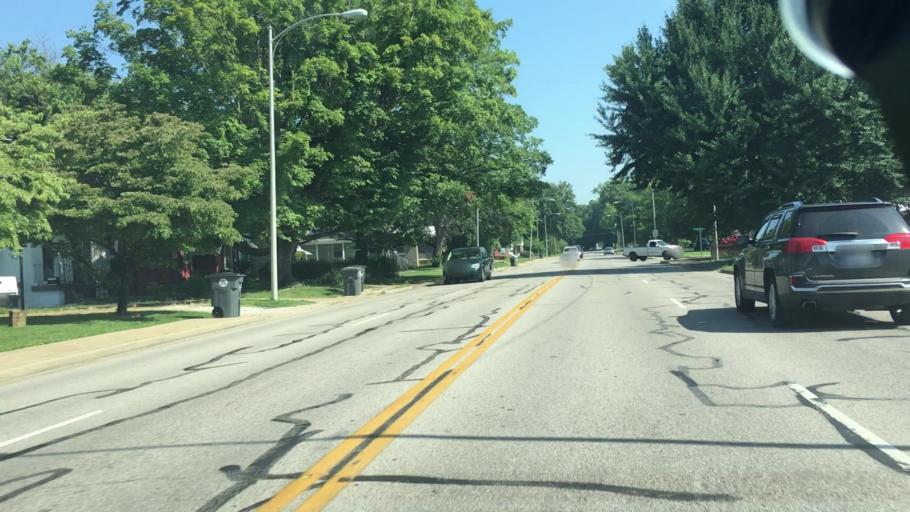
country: US
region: Indiana
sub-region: Vanderburgh County
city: Evansville
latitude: 37.9934
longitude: -87.5291
